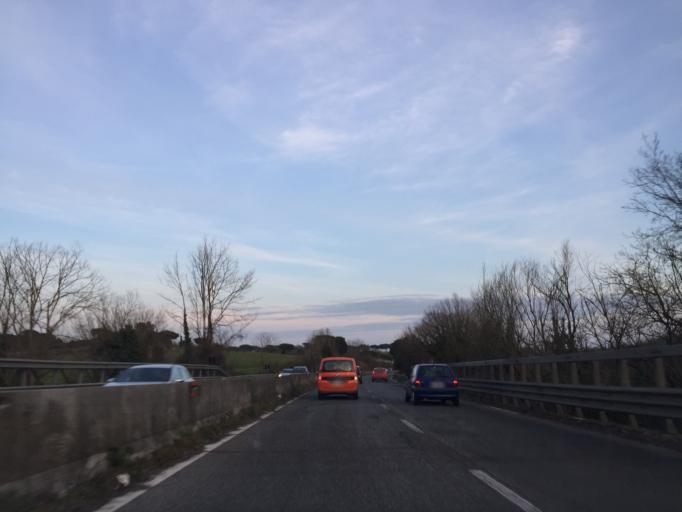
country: IT
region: Latium
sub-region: Citta metropolitana di Roma Capitale
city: Formello
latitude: 42.0427
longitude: 12.4173
